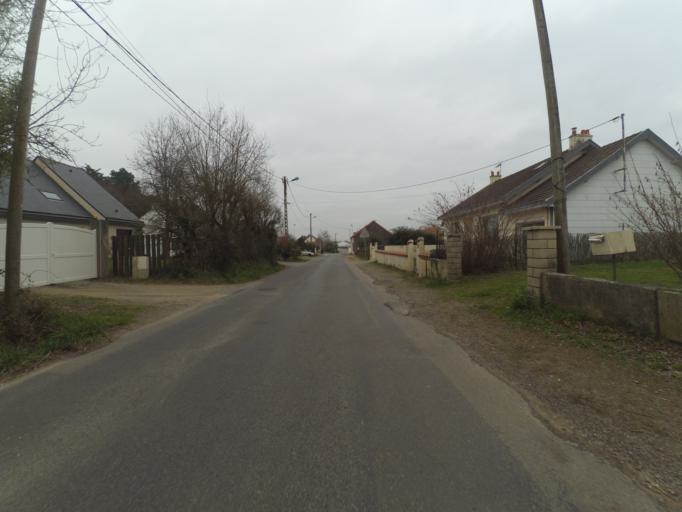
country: FR
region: Pays de la Loire
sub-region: Departement de la Loire-Atlantique
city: Indre
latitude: 47.2259
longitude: -1.6797
